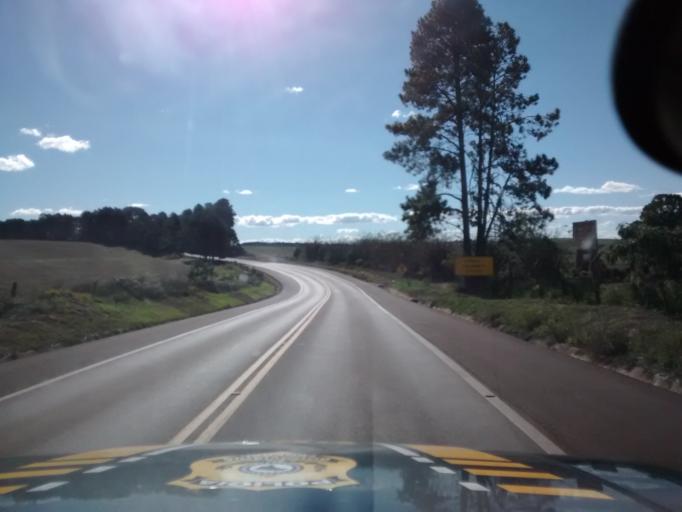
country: BR
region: Rio Grande do Sul
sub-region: Lagoa Vermelha
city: Lagoa Vermelha
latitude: -28.3067
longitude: -51.3674
